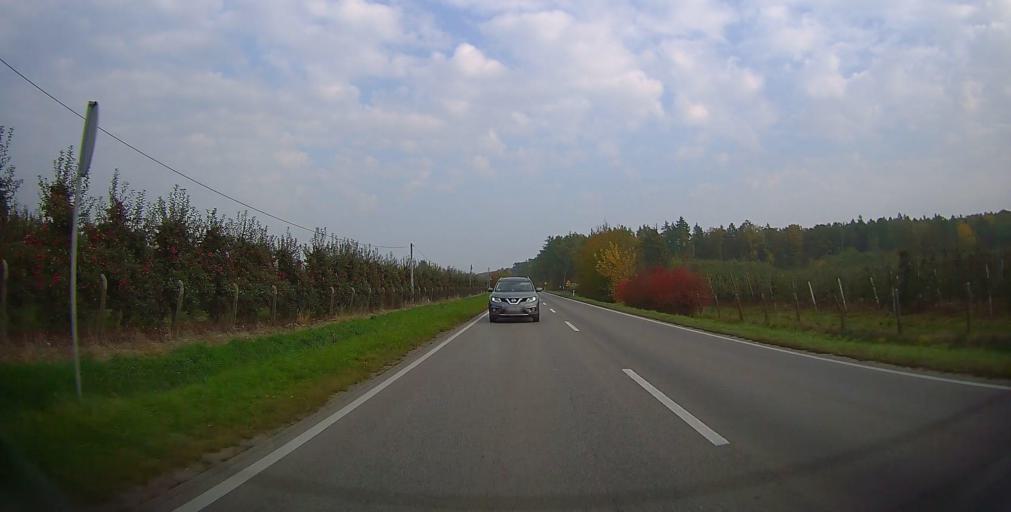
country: PL
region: Masovian Voivodeship
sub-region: Powiat grojecki
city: Belsk Duzy
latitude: 51.7886
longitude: 20.7808
